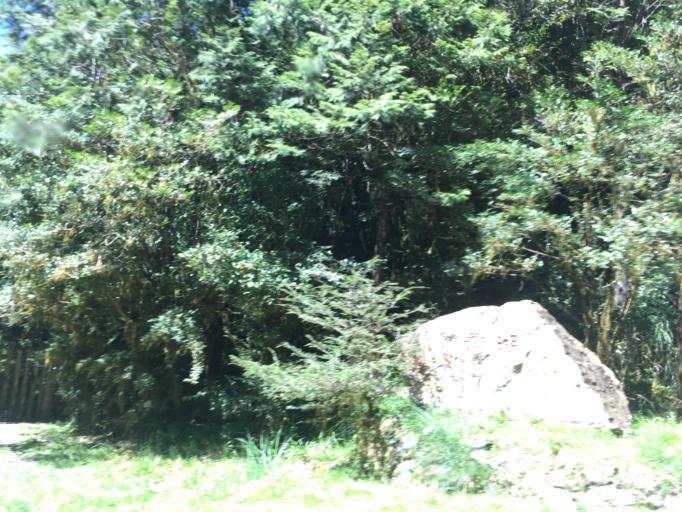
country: TW
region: Taiwan
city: Daxi
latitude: 24.5774
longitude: 121.4119
